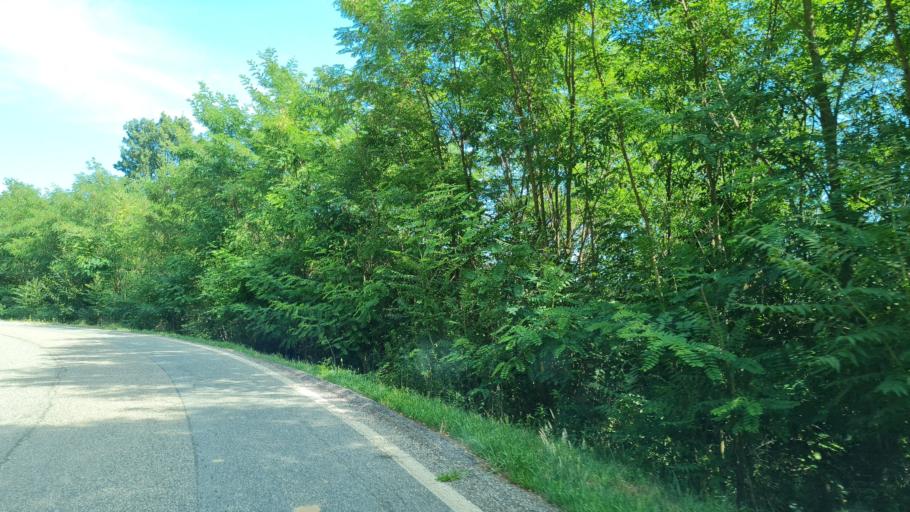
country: IT
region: Piedmont
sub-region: Provincia di Biella
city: Lessona
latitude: 45.5915
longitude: 8.2065
